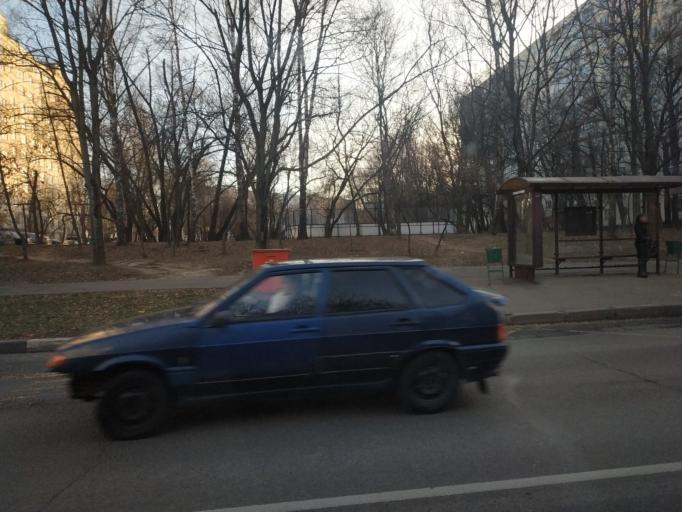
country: RU
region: Moskovskaya
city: Biryulevo Zapadnoye
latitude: 55.6009
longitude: 37.6199
